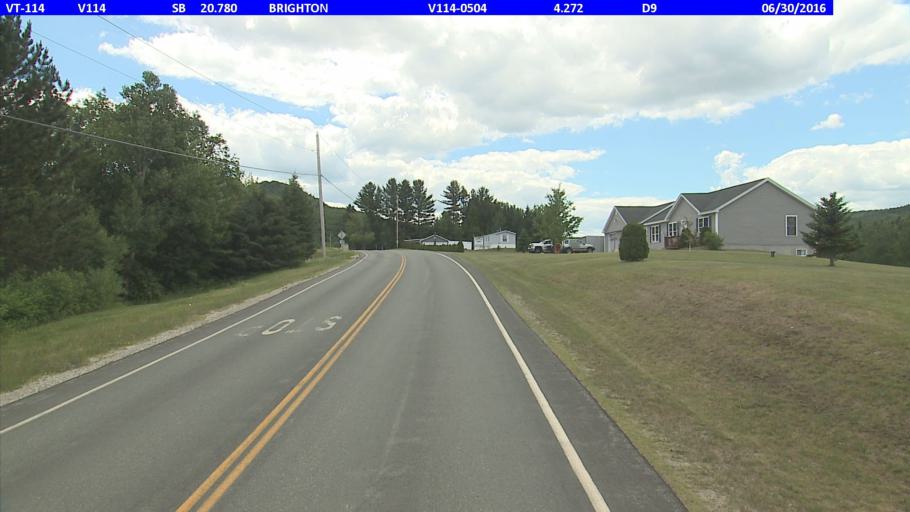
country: US
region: Vermont
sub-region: Caledonia County
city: Lyndonville
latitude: 44.7948
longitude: -71.9104
